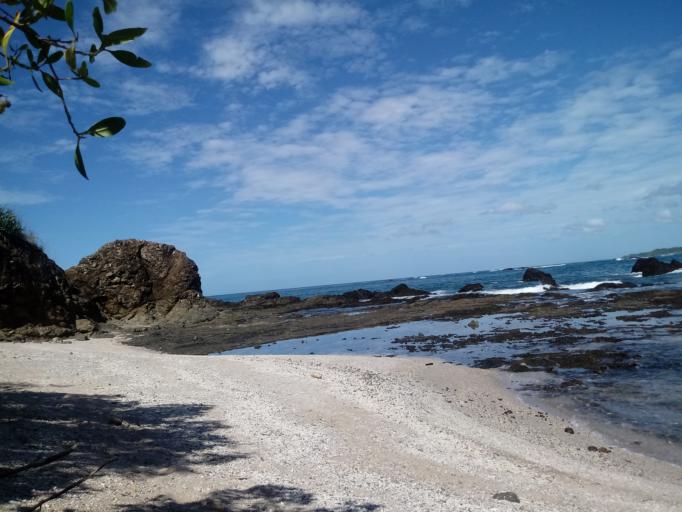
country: CR
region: Guanacaste
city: Samara
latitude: 10.0310
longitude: -85.7425
